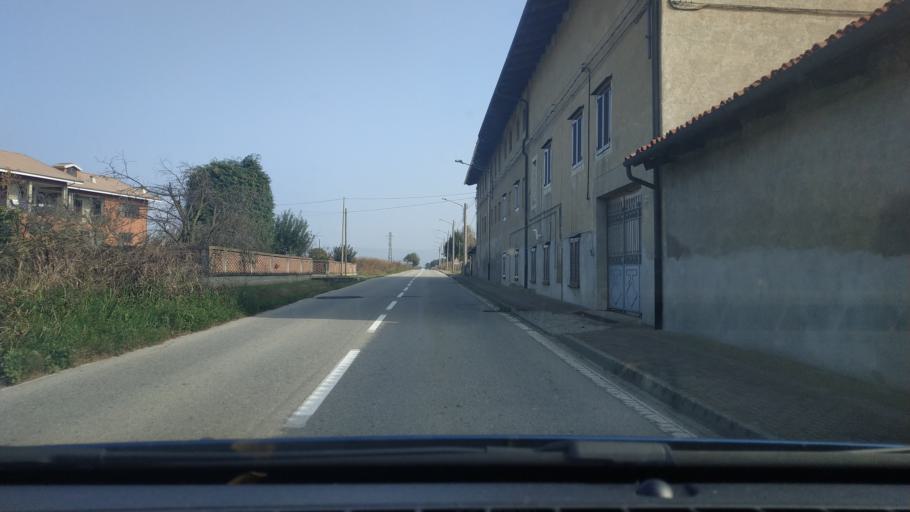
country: IT
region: Piedmont
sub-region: Provincia di Torino
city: Romano Canavese
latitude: 45.4046
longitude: 7.8718
